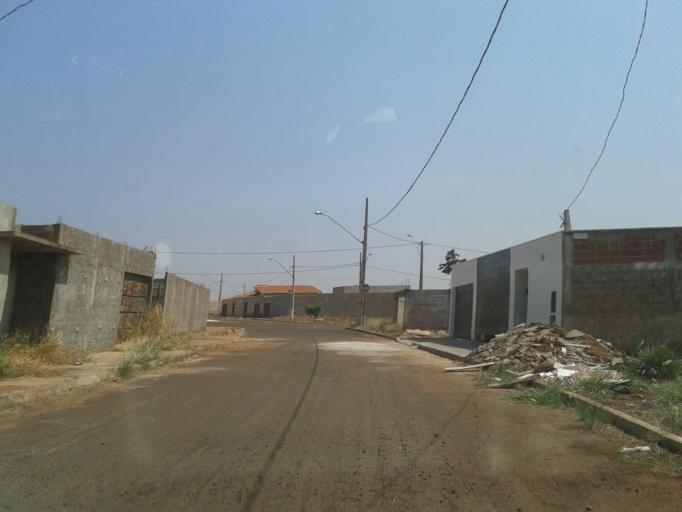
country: BR
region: Minas Gerais
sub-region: Ituiutaba
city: Ituiutaba
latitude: -18.9615
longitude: -49.4401
